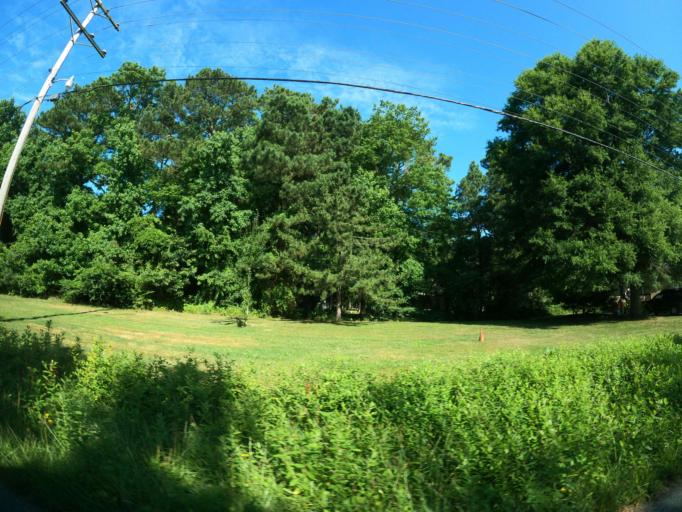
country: US
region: Delaware
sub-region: Sussex County
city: Ocean View
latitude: 38.5220
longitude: -75.0967
